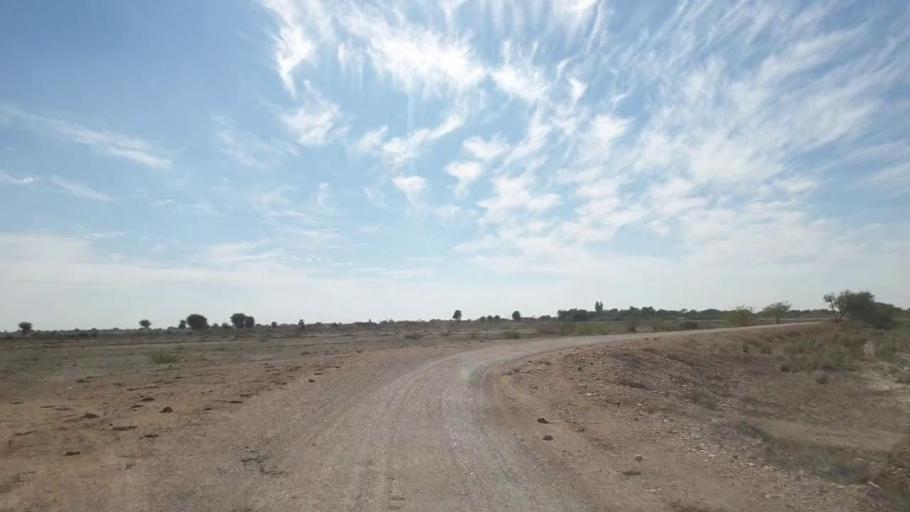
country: PK
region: Sindh
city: Pithoro
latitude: 25.5709
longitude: 69.3049
